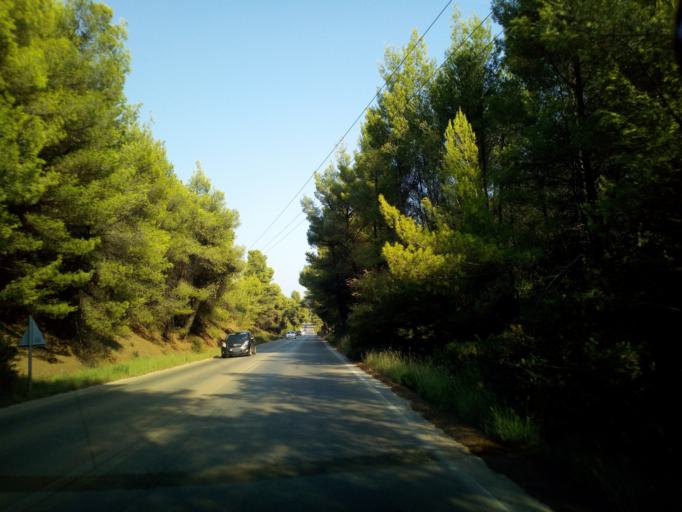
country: GR
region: Central Macedonia
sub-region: Nomos Chalkidikis
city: Nikiti
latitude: 40.2298
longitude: 23.6305
